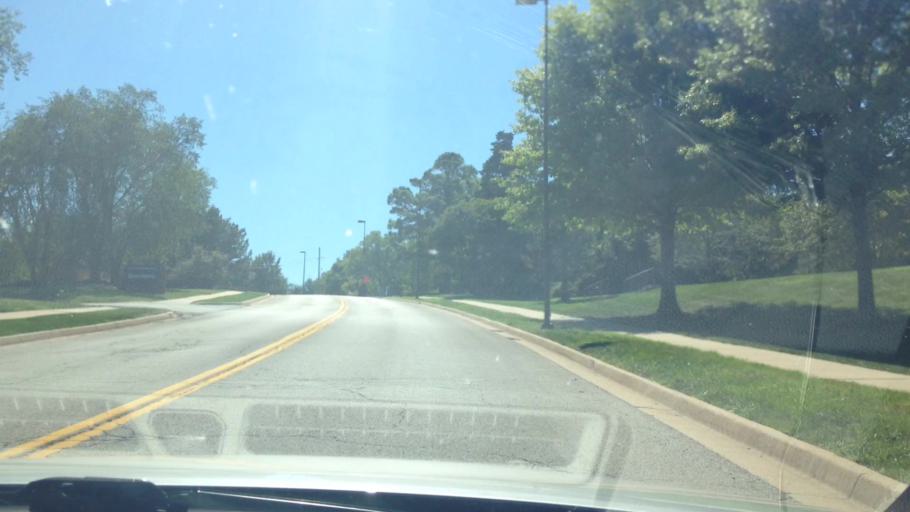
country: US
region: Missouri
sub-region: Jackson County
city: Raytown
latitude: 39.0067
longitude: -94.5048
